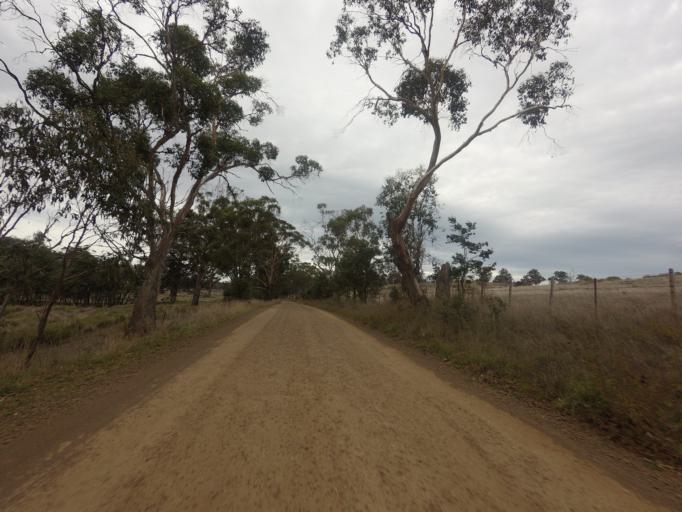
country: AU
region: Tasmania
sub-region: Derwent Valley
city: New Norfolk
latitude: -42.5619
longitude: 146.9242
